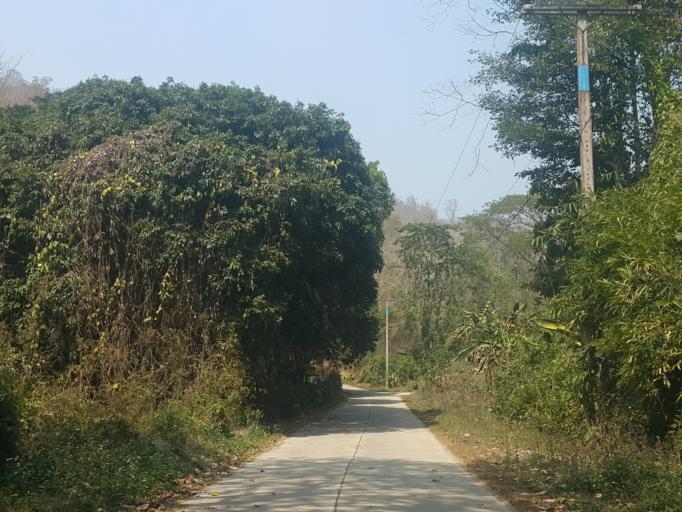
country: TH
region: Chiang Mai
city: Hang Dong
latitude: 18.7326
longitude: 98.8289
